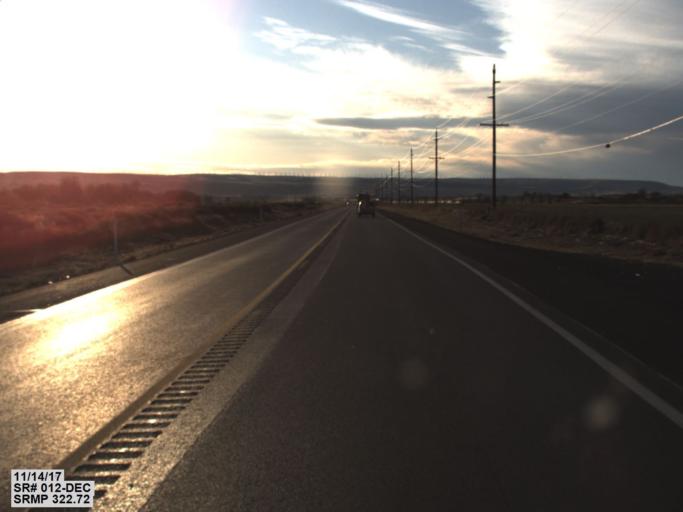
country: US
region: Washington
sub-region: Walla Walla County
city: Garrett
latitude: 46.0523
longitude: -118.6188
